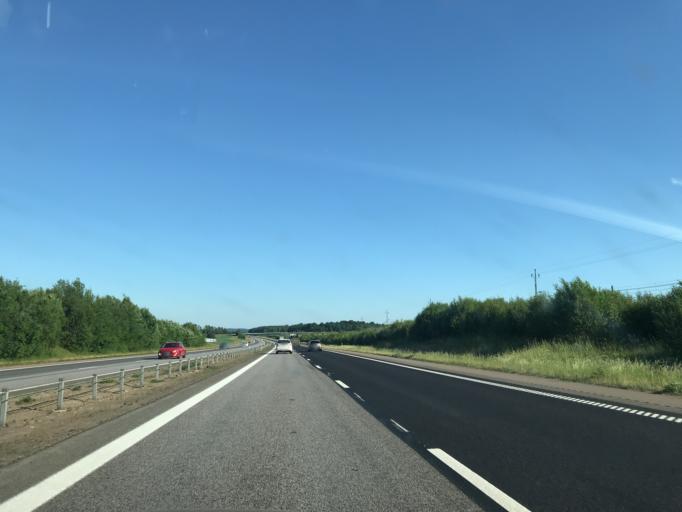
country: SE
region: Halland
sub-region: Halmstads Kommun
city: Aled
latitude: 56.7321
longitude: 12.8773
